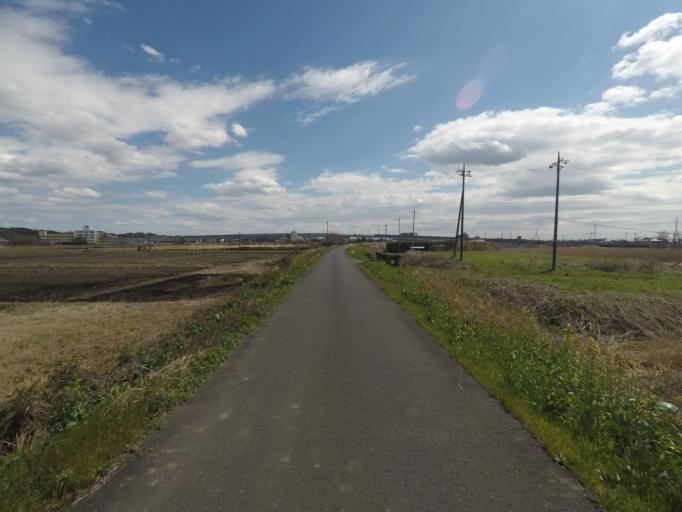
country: JP
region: Ibaraki
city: Fujishiro
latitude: 35.9383
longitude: 140.1285
